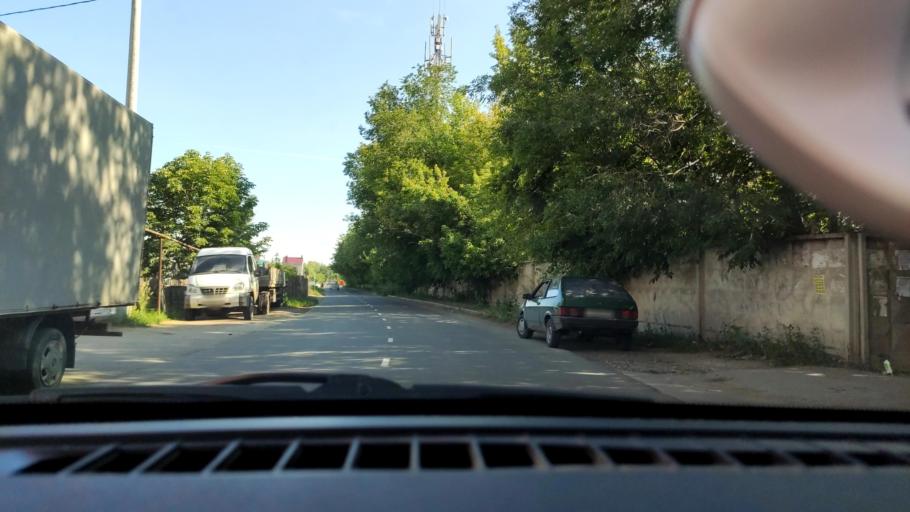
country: RU
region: Samara
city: Smyshlyayevka
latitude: 53.2107
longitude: 50.3276
